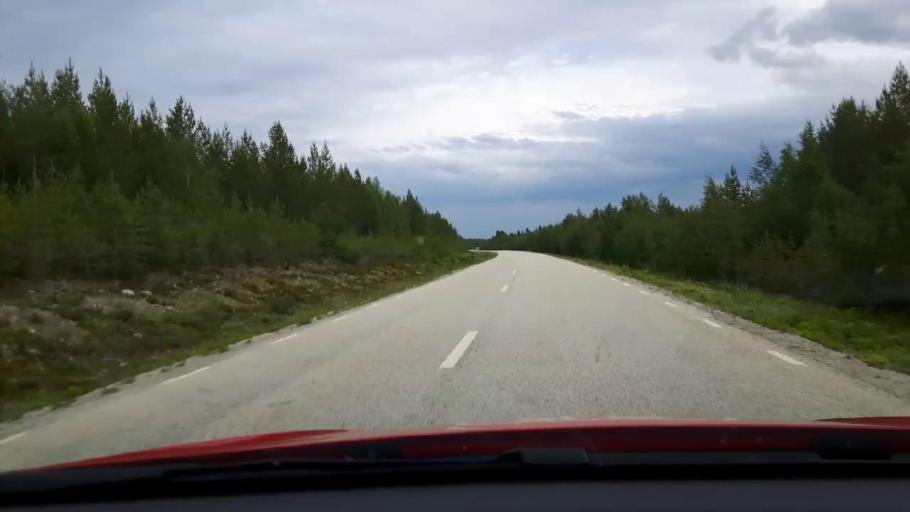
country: SE
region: Jaemtland
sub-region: Bergs Kommun
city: Hoverberg
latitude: 62.6986
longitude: 13.9606
